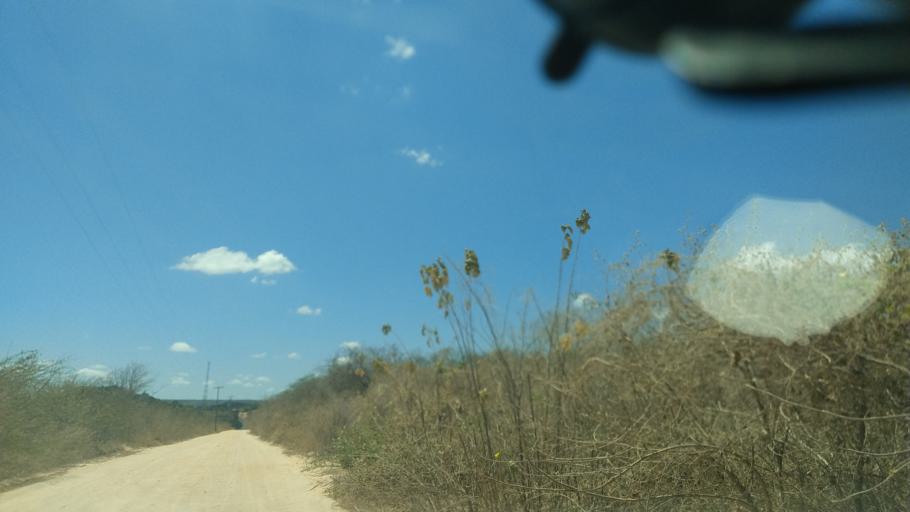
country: BR
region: Rio Grande do Norte
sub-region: Cerro Cora
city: Cerro Cora
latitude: -6.0284
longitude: -36.3386
